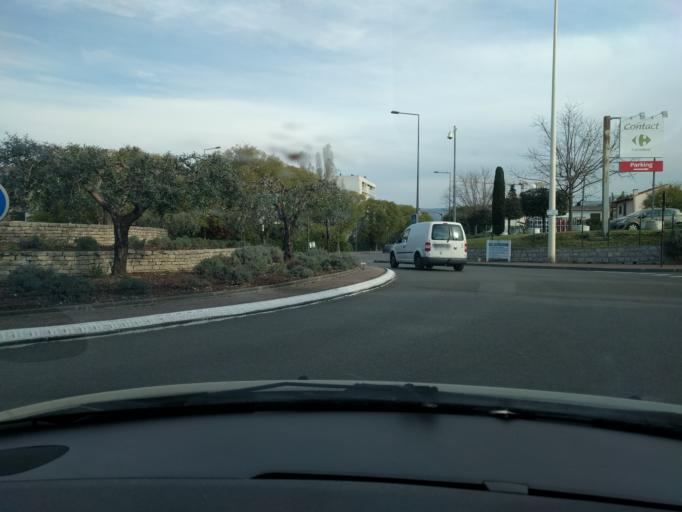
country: FR
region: Provence-Alpes-Cote d'Azur
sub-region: Departement des Alpes-Maritimes
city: Mandelieu-la-Napoule
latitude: 43.5570
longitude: 6.9689
